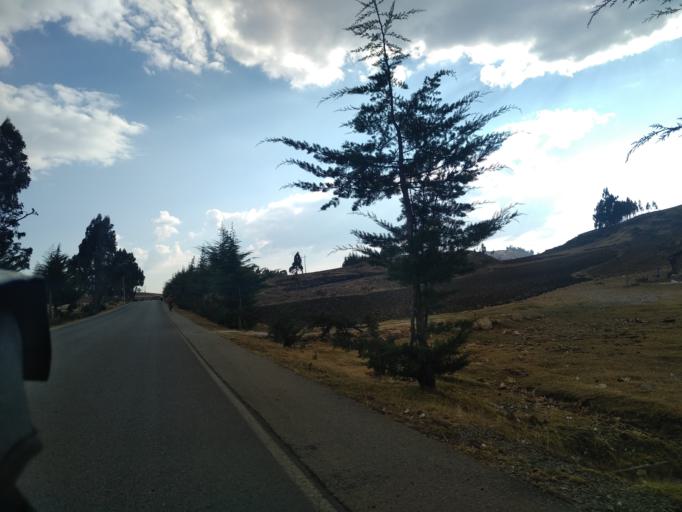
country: PE
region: Cajamarca
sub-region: Provincia de Cajamarca
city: Llacanora
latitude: -7.1445
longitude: -78.3938
